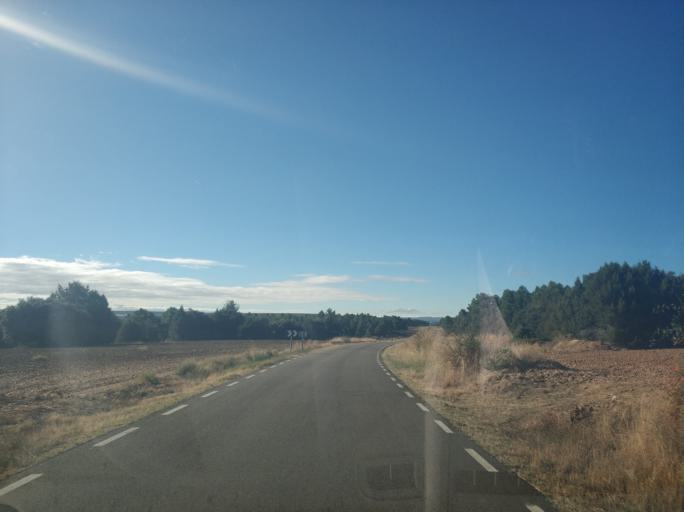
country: ES
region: Castille and Leon
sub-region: Provincia de Burgos
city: San Juan del Monte
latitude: 41.6699
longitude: -3.5272
